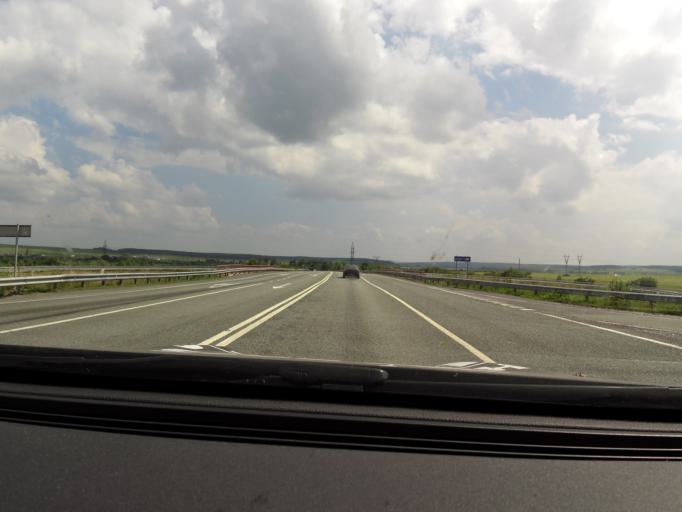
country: RU
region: Sverdlovsk
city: Achit
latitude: 56.7898
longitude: 57.8808
